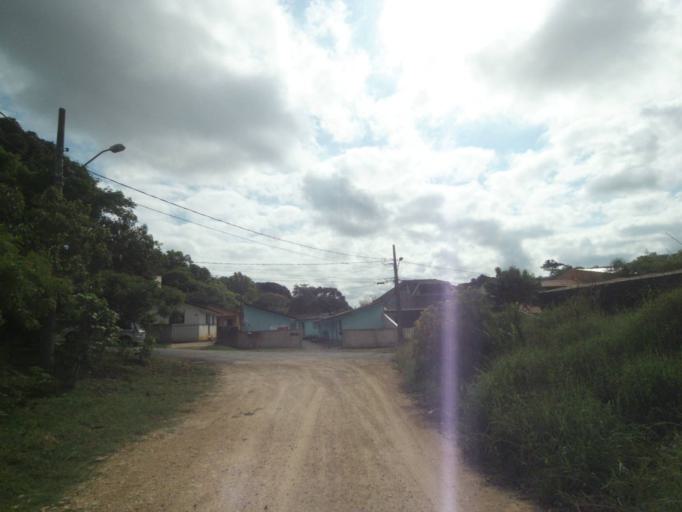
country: BR
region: Parana
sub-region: Curitiba
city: Curitiba
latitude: -25.3790
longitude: -49.2974
